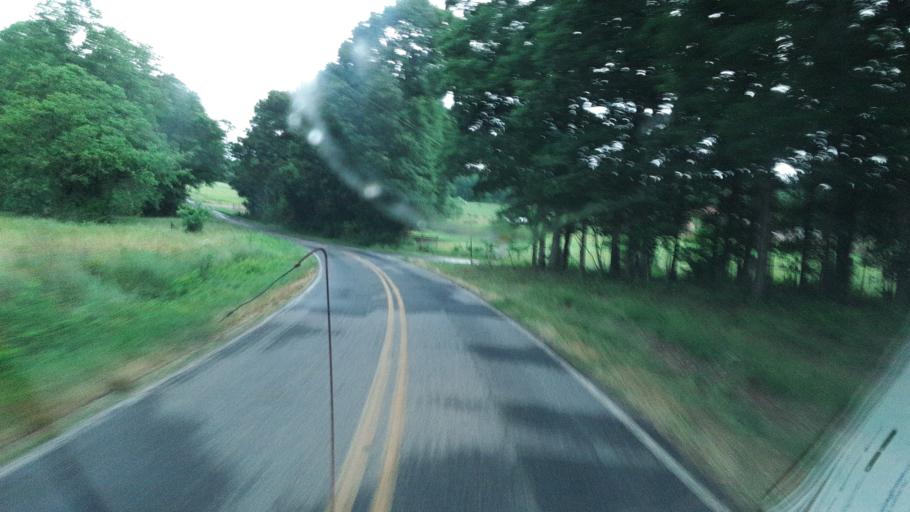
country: US
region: North Carolina
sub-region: Yadkin County
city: Jonesville
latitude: 36.1075
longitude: -80.8833
